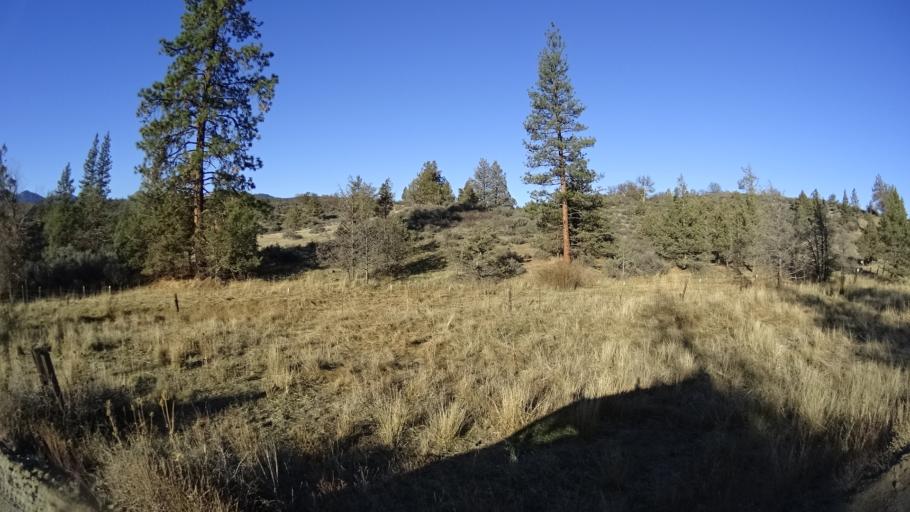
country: US
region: Oregon
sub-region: Jackson County
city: Ashland
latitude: 41.9857
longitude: -122.6232
